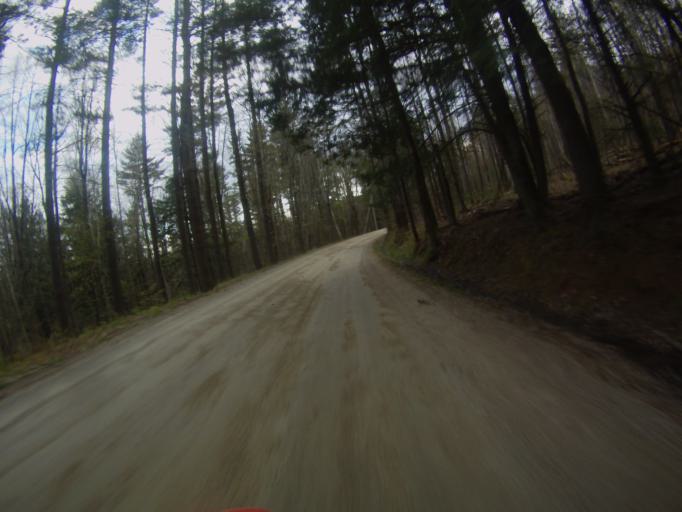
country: US
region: Vermont
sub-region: Addison County
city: Middlebury (village)
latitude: 43.9817
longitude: -73.0564
